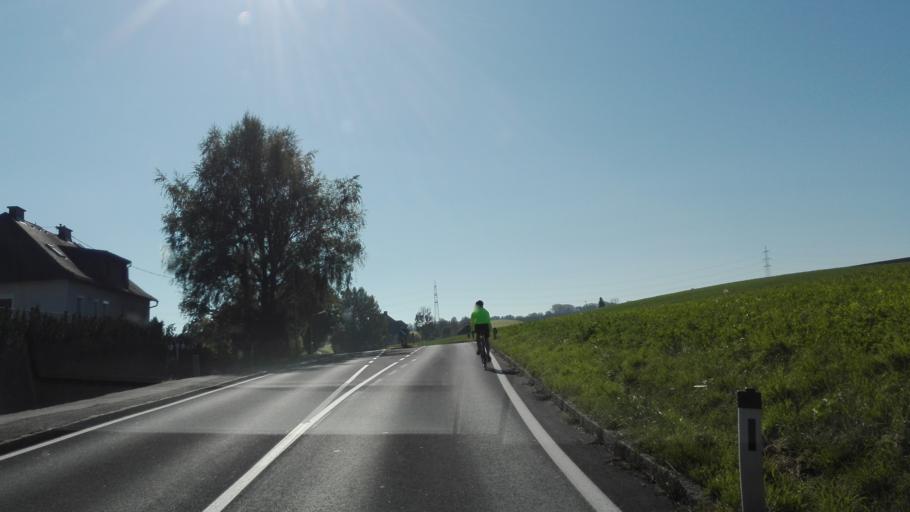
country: AT
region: Upper Austria
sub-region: Politischer Bezirk Linz-Land
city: Pasching
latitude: 48.2821
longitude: 14.2019
